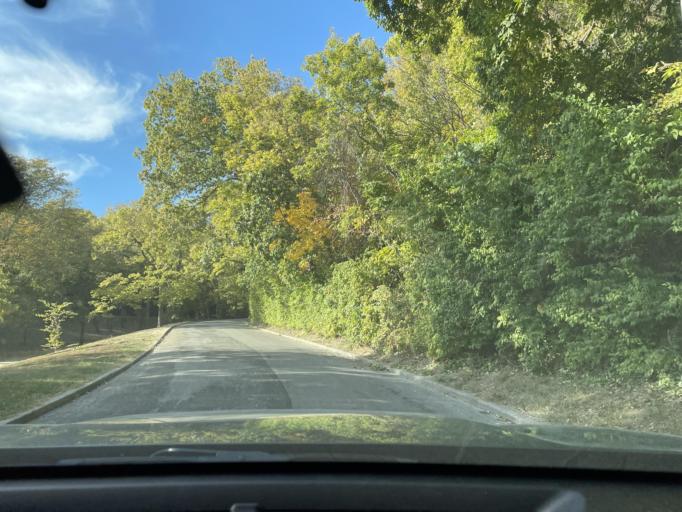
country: US
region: Missouri
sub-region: Buchanan County
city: Saint Joseph
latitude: 39.7999
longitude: -94.8479
